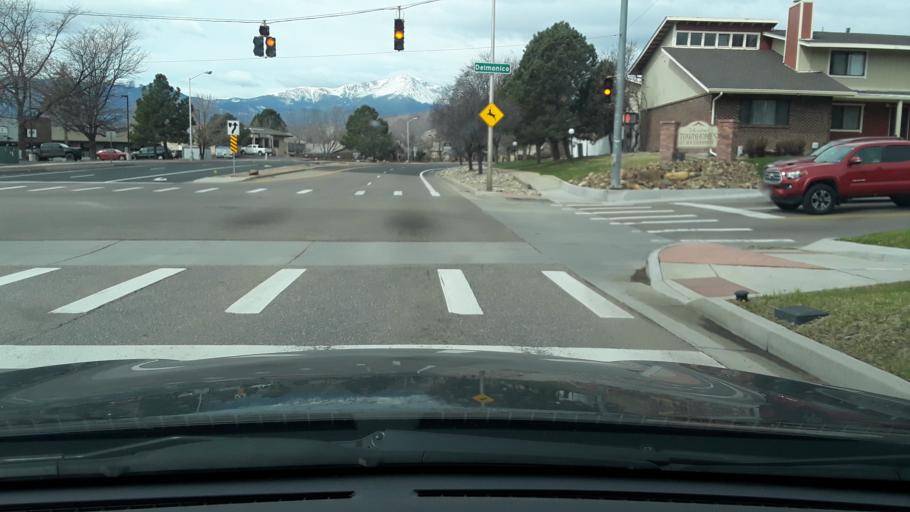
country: US
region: Colorado
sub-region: El Paso County
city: Air Force Academy
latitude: 38.9287
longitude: -104.8306
